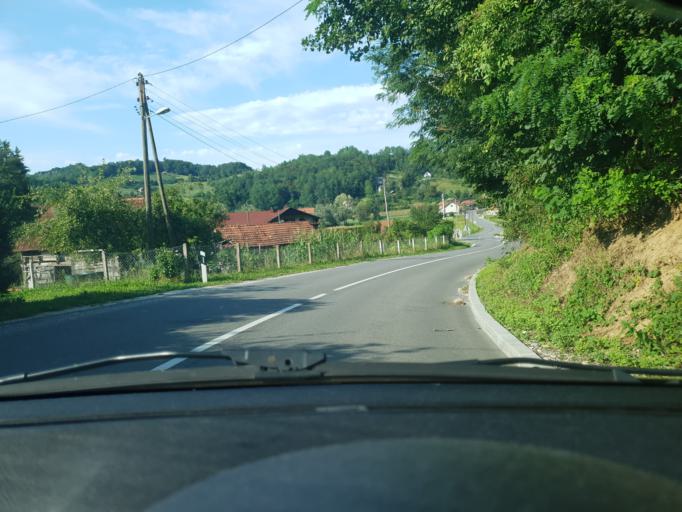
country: HR
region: Krapinsko-Zagorska
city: Pregrada
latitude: 46.0775
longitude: 15.8018
